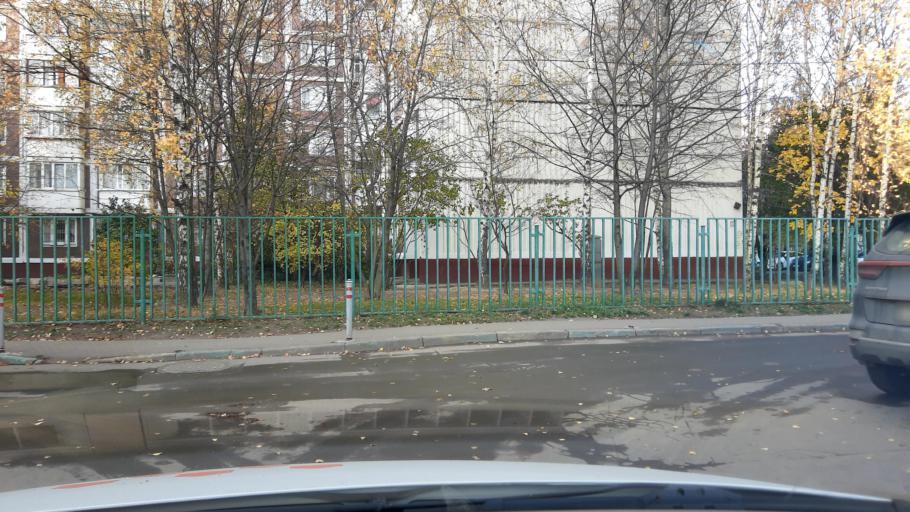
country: RU
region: Moskovskaya
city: Shcherbinka
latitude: 55.5485
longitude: 37.5504
